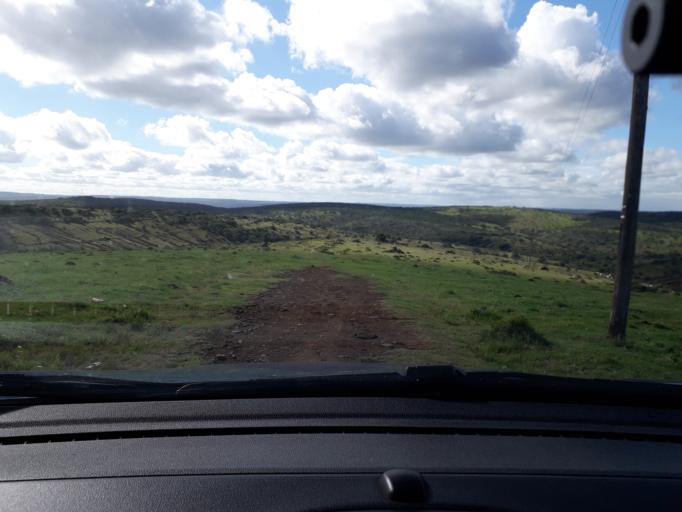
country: ZA
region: Eastern Cape
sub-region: Buffalo City Metropolitan Municipality
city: Bhisho
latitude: -33.1092
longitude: 27.4299
